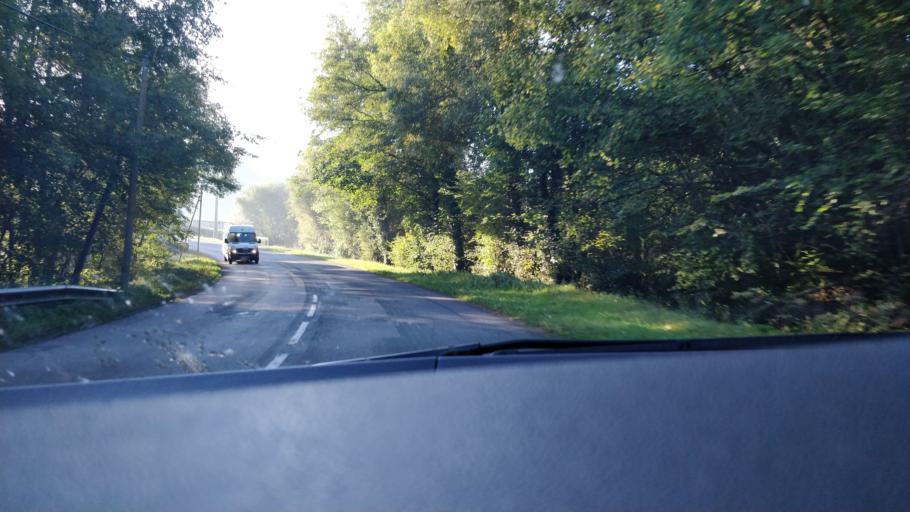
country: FR
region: Limousin
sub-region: Departement de la Creuse
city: Bourganeuf
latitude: 45.9563
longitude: 1.7411
